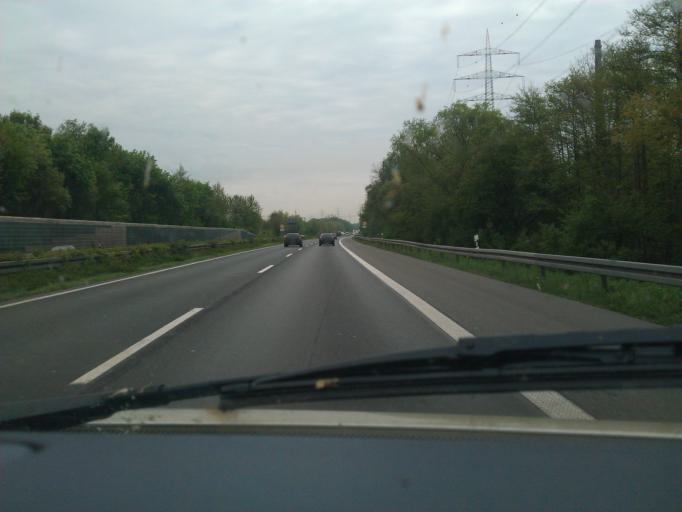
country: DE
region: North Rhine-Westphalia
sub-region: Regierungsbezirk Munster
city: Bottrop
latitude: 51.5676
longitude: 6.9300
